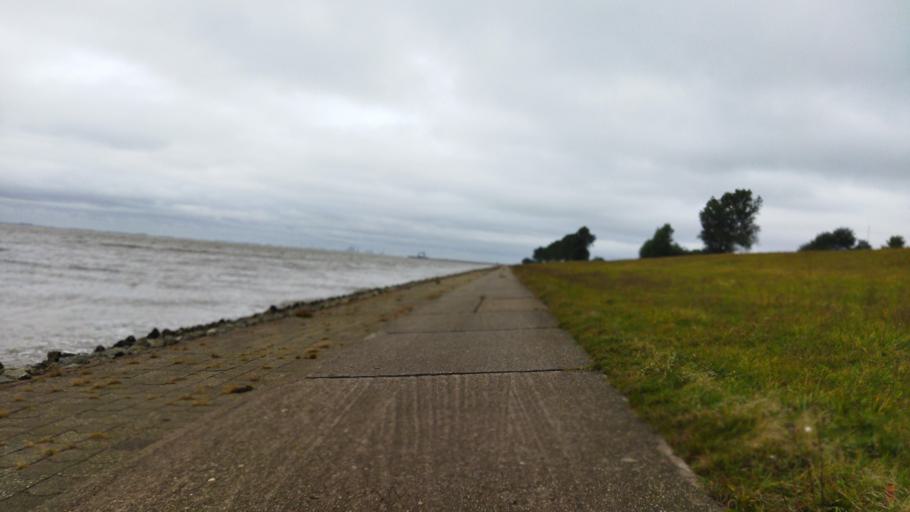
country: NL
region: Groningen
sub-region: Gemeente Delfzijl
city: Delfzijl
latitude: 53.3436
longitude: 7.0143
